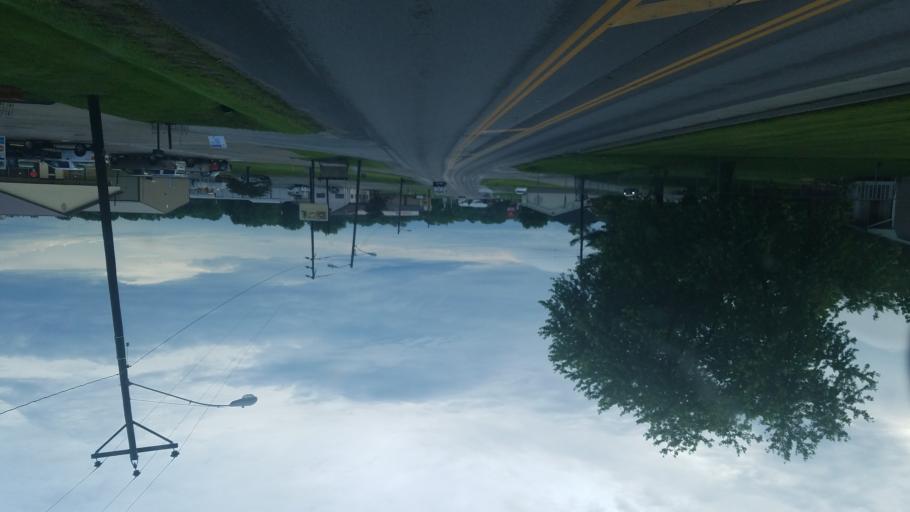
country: US
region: Missouri
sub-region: Moniteau County
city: California
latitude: 38.6293
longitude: -92.5781
